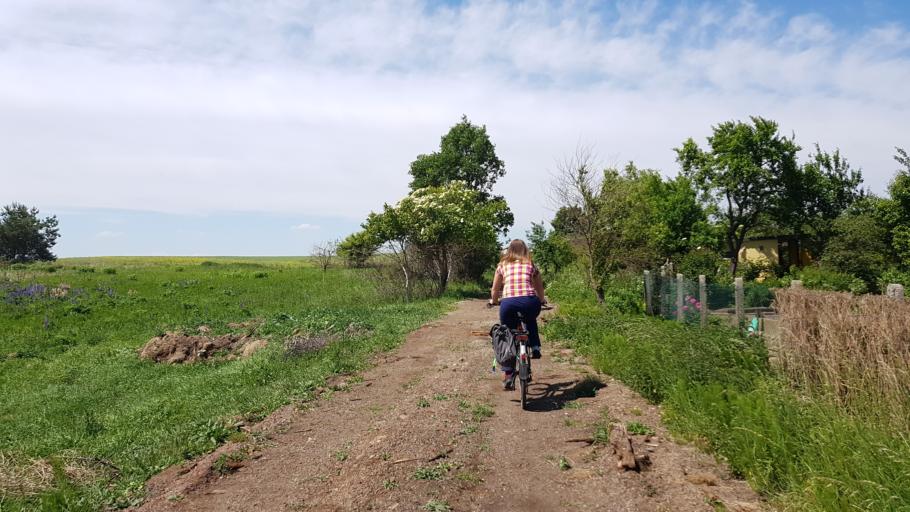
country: PL
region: West Pomeranian Voivodeship
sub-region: Powiat mysliborski
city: Barlinek
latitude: 52.9900
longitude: 15.1966
